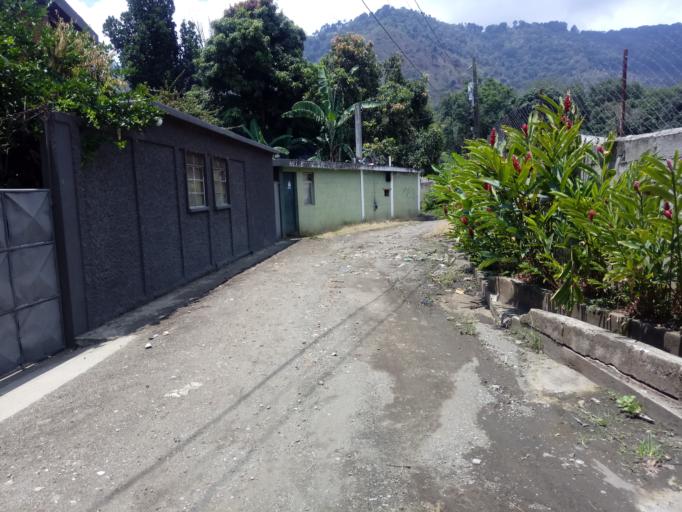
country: GT
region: Guatemala
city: Villa Canales
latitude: 14.4251
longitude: -90.5516
